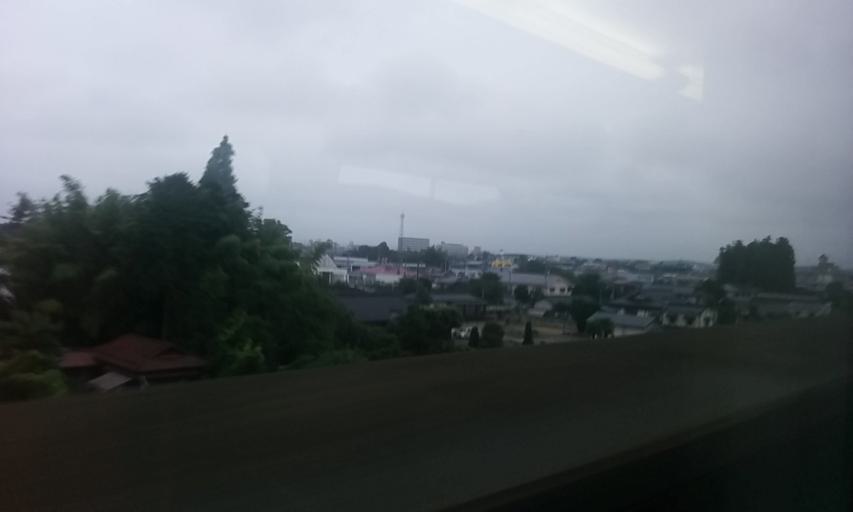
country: JP
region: Tochigi
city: Kuroiso
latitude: 36.9591
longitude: 140.0502
